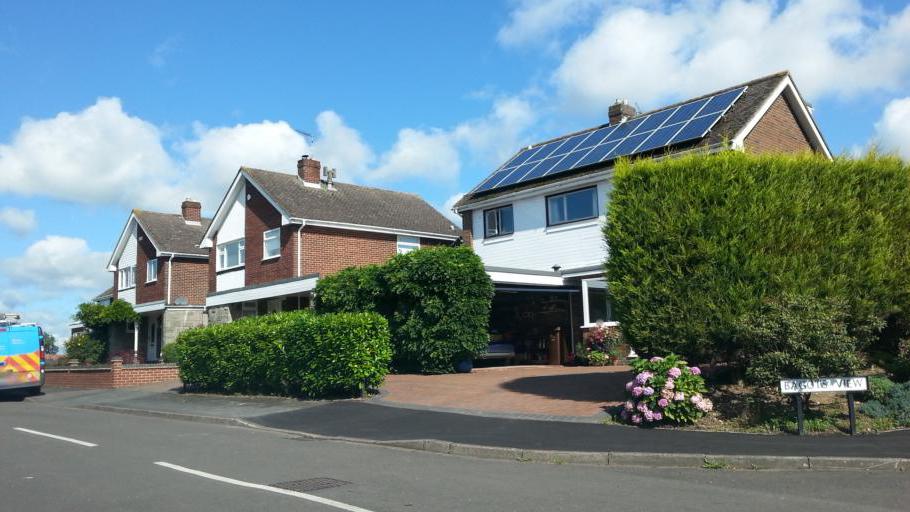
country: GB
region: England
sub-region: Staffordshire
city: Uttoxeter
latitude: 52.8212
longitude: -1.8800
